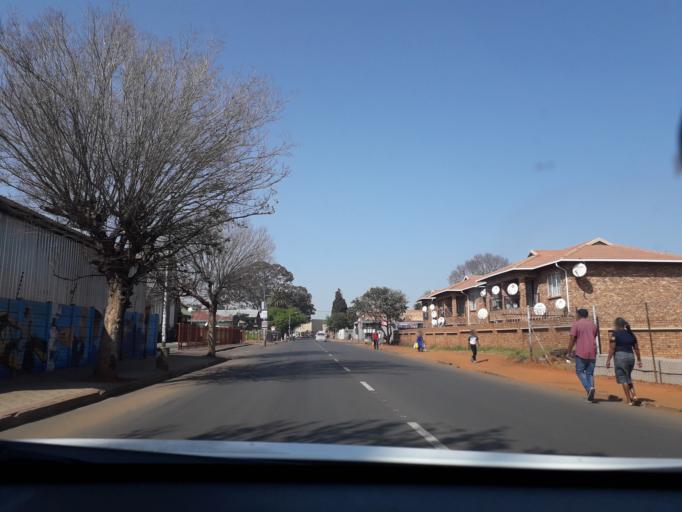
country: ZA
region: Gauteng
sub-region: City of Johannesburg Metropolitan Municipality
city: Modderfontein
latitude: -26.1041
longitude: 28.2382
